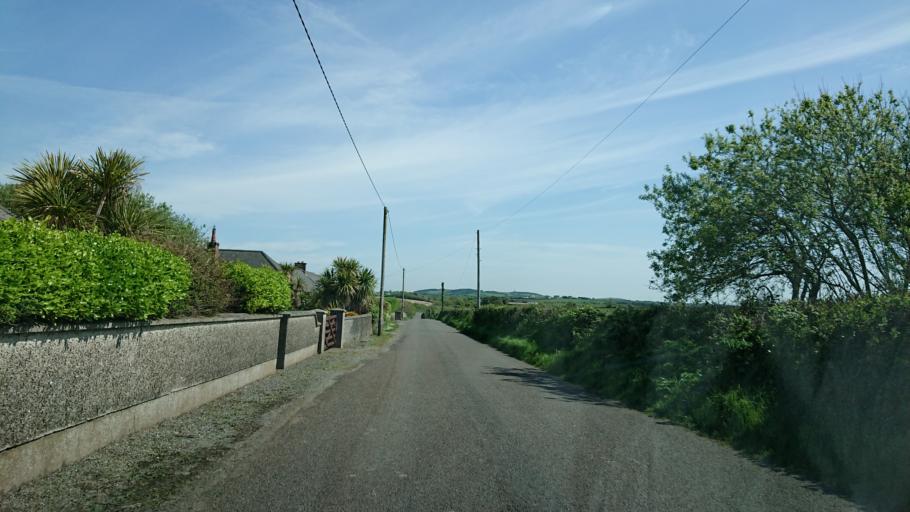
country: IE
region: Munster
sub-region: Waterford
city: Dunmore East
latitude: 52.1568
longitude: -7.0685
